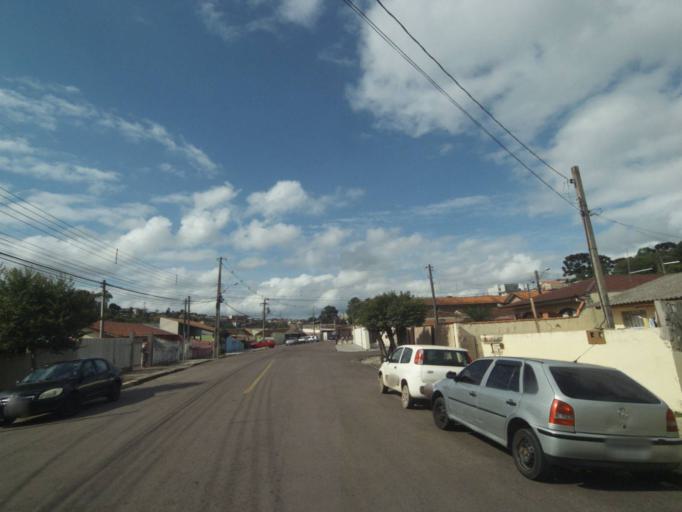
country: BR
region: Parana
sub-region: Curitiba
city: Curitiba
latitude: -25.3824
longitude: -49.3013
